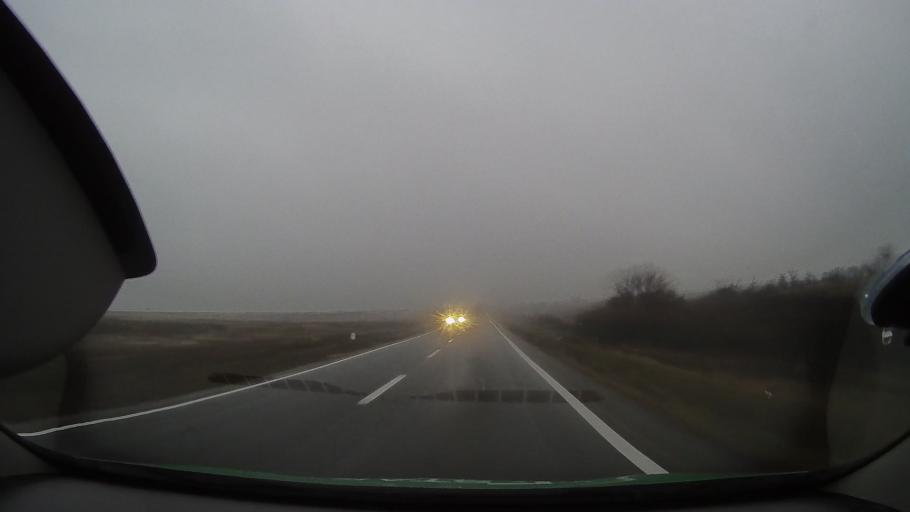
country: RO
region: Arad
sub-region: Comuna Craiova
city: Craiova
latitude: 46.6263
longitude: 21.9586
